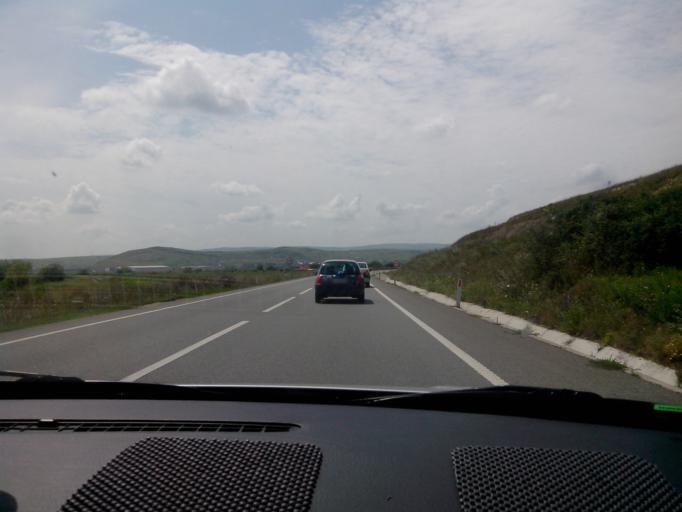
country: RO
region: Cluj
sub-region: Comuna Apahida
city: Apahida
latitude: 46.8097
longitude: 23.7355
